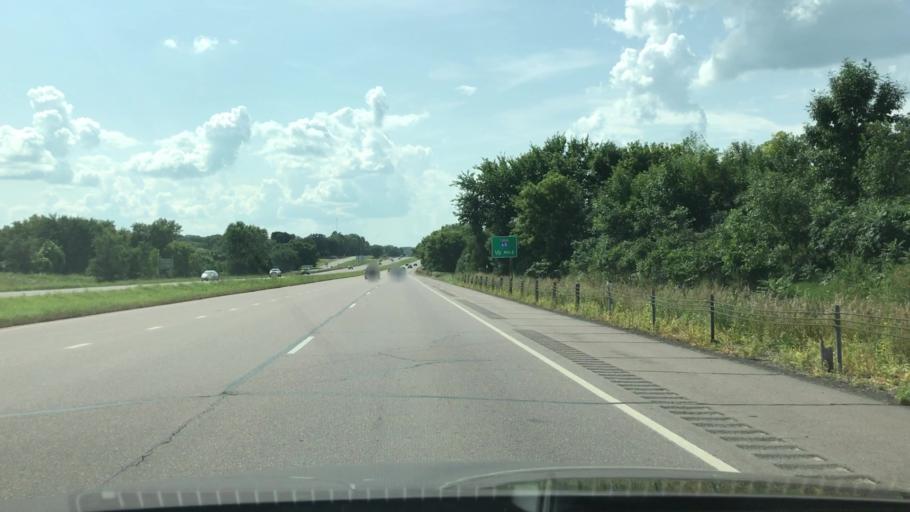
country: US
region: Minnesota
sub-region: Nicollet County
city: North Mankato
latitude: 44.1525
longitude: -94.0514
